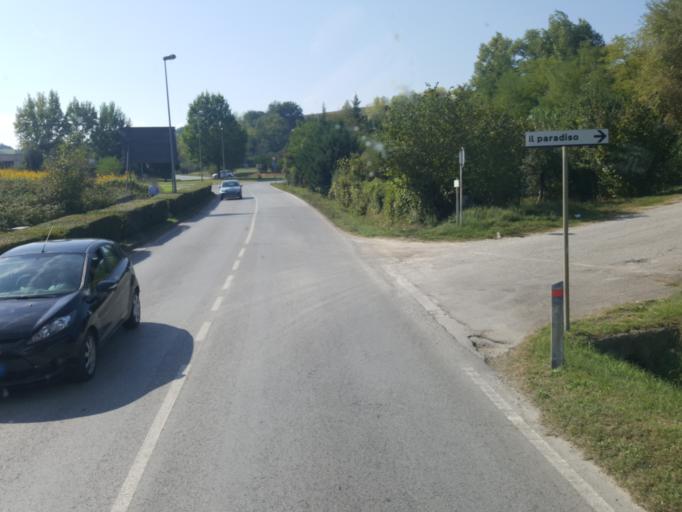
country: IT
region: Tuscany
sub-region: Provincia di Siena
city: Colle di Val d'Elsa
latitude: 43.4154
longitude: 11.1301
